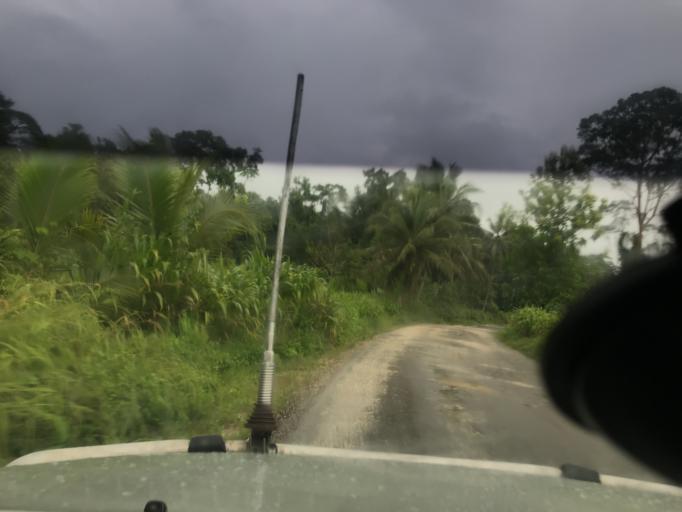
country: SB
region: Malaita
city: Auki
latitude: -8.9896
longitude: 160.7874
